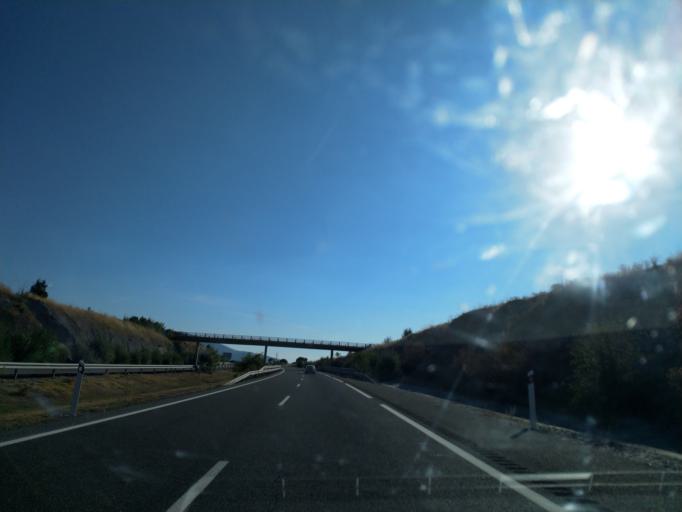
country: ES
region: Castille and Leon
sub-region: Provincia de Segovia
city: Segovia
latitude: 40.8943
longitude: -4.1118
